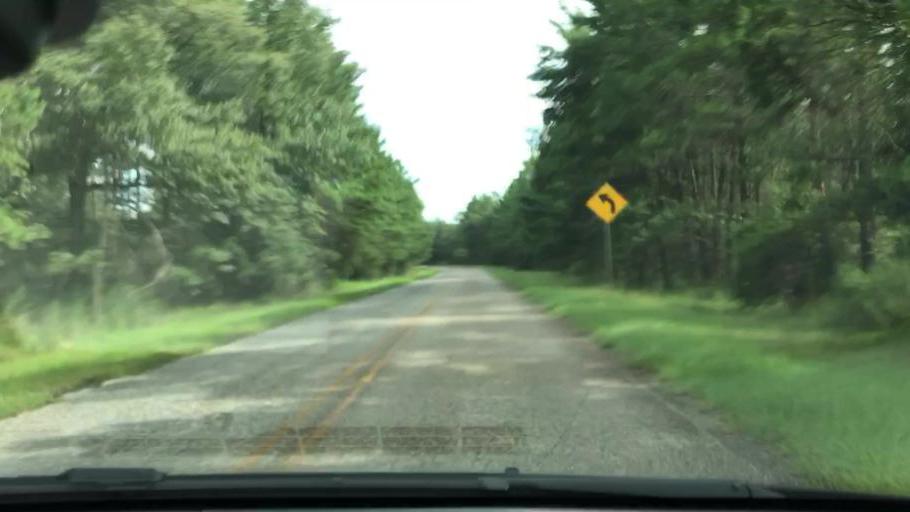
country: US
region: Georgia
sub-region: Early County
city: Blakely
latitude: 31.5116
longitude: -84.9524
